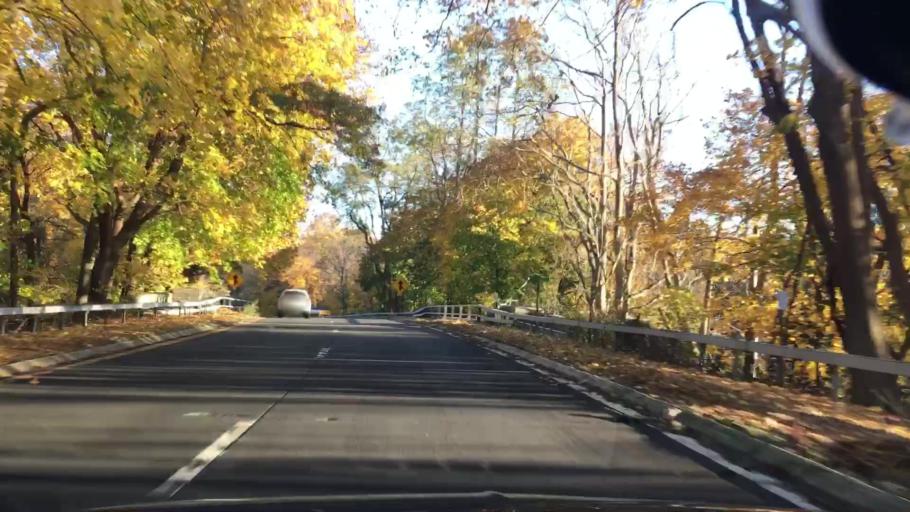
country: US
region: New York
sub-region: Westchester County
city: Hawthorne
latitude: 41.1075
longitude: -73.8009
